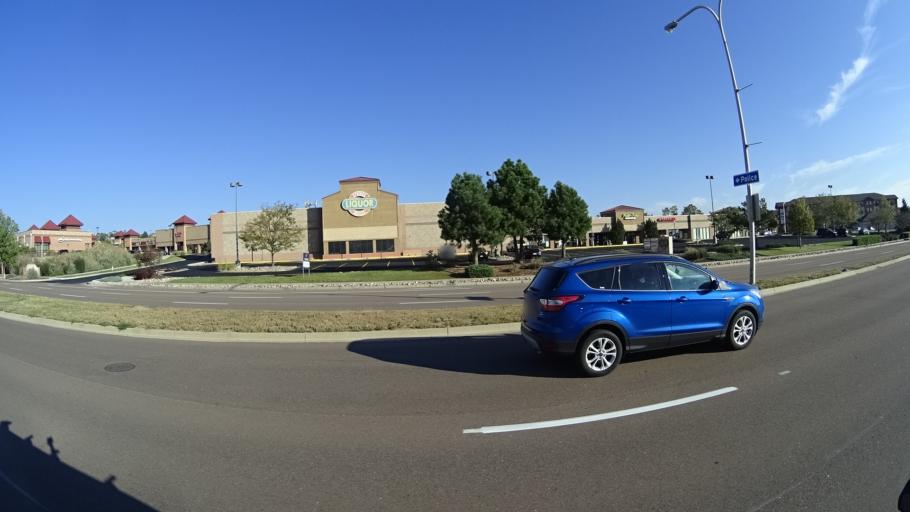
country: US
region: Colorado
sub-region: El Paso County
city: Cimarron Hills
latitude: 38.8853
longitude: -104.7143
